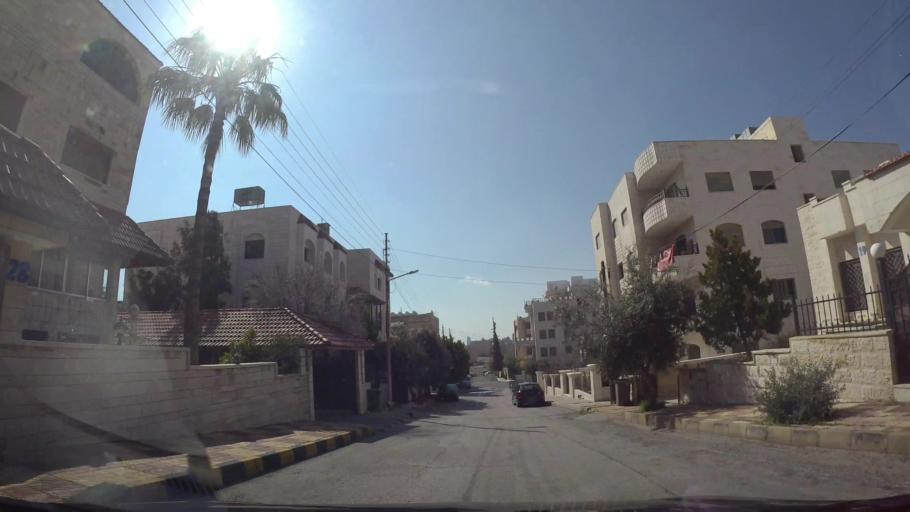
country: JO
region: Amman
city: Al Jubayhah
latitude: 31.9976
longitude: 35.8987
